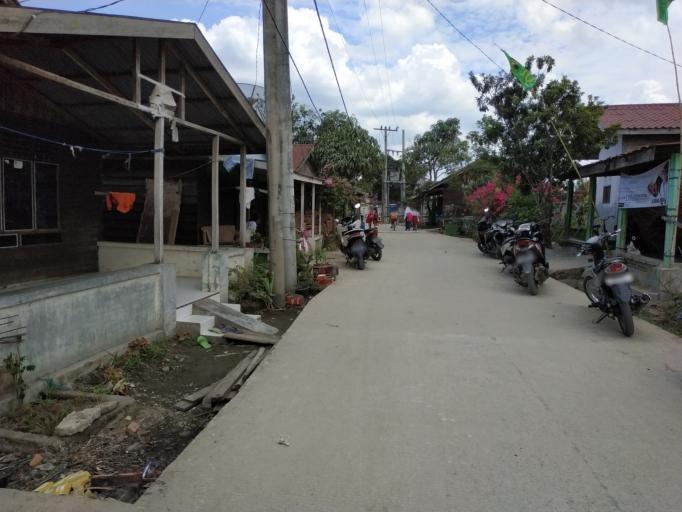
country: ID
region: North Sumatra
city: Tanjungbalai
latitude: 2.9586
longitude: 99.8154
